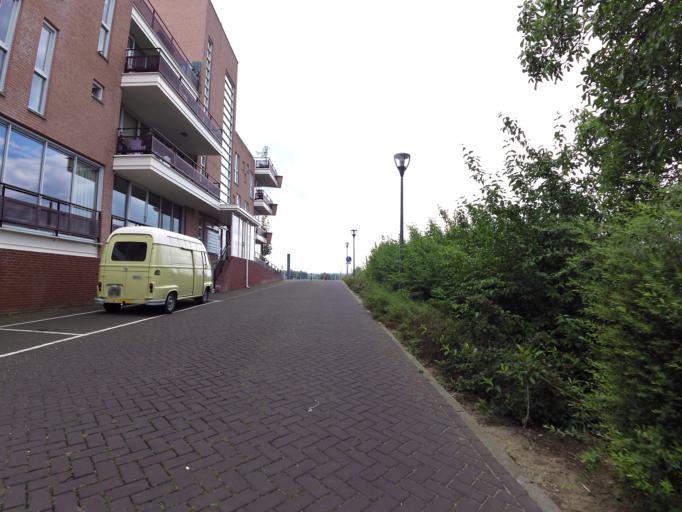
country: NL
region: Gelderland
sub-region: Gemeente Doesburg
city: Doesburg
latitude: 52.0151
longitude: 6.1290
